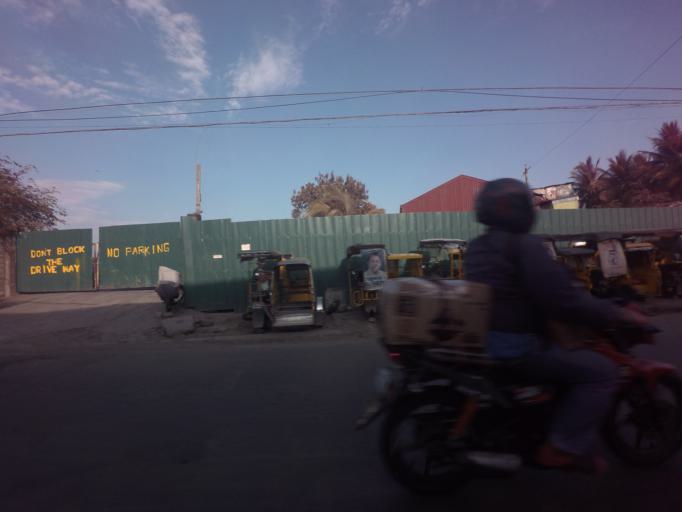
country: PH
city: Sambayanihan People's Village
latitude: 14.4983
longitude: 121.0048
